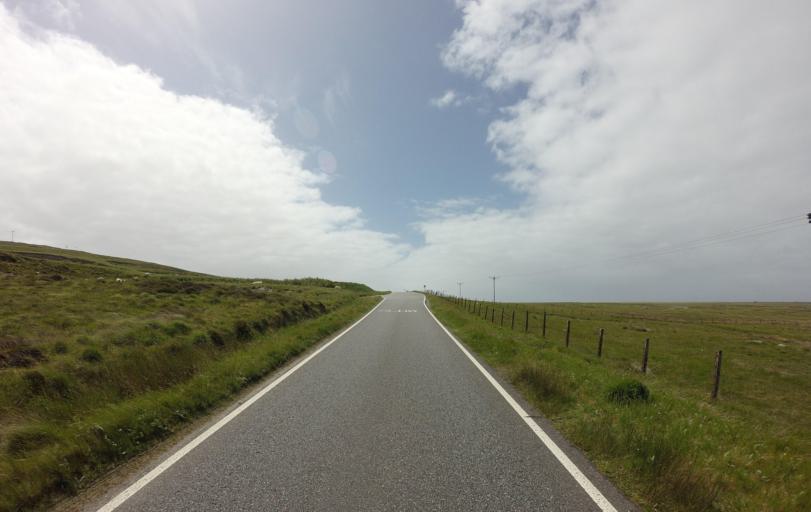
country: GB
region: Scotland
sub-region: Eilean Siar
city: Benbecula
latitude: 57.3465
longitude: -7.3618
